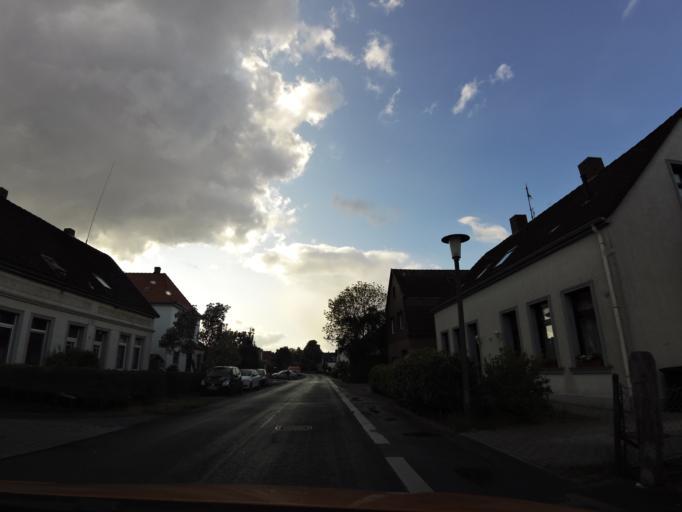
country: DE
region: Lower Saxony
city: Oldenburg
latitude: 53.1307
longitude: 8.2400
